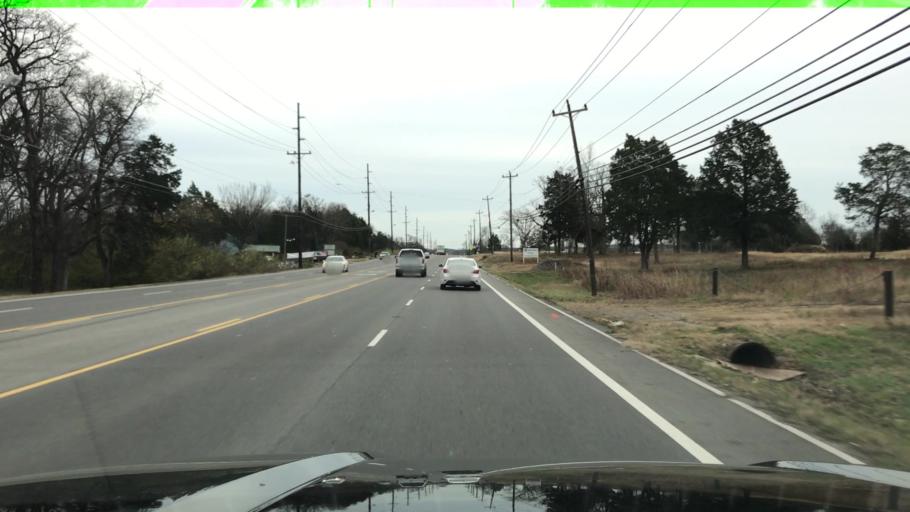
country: US
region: Tennessee
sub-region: Rutherford County
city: La Vergne
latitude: 36.0346
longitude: -86.5976
